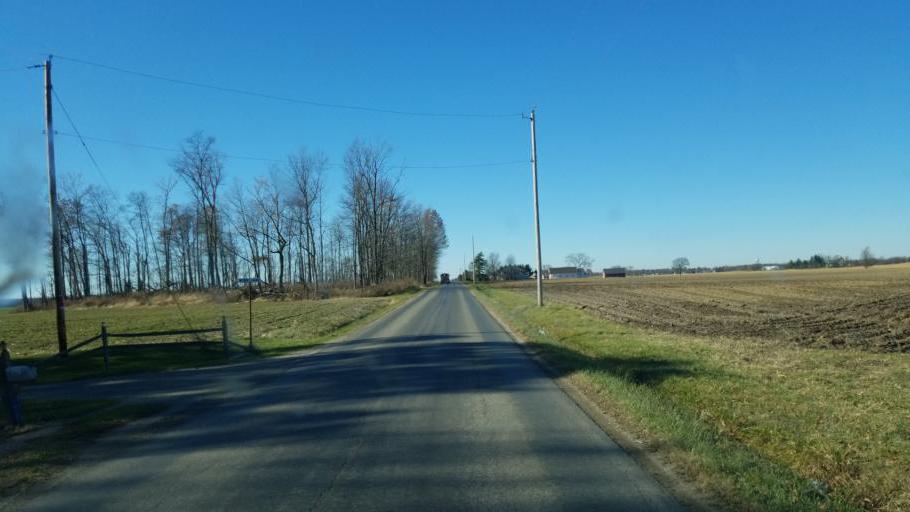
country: US
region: Ohio
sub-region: Huron County
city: Greenwich
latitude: 40.9602
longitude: -82.5733
